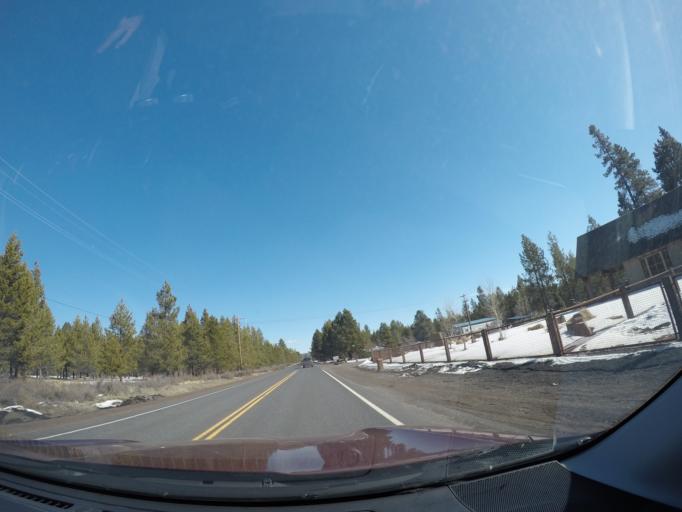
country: US
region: Oregon
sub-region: Deschutes County
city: Sunriver
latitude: 43.8630
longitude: -121.4656
